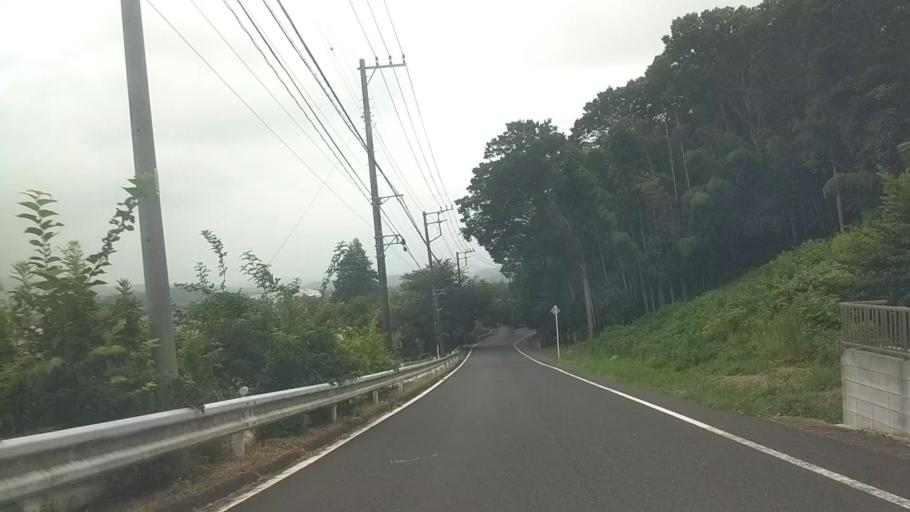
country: JP
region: Chiba
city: Futtsu
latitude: 35.2192
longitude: 139.8754
